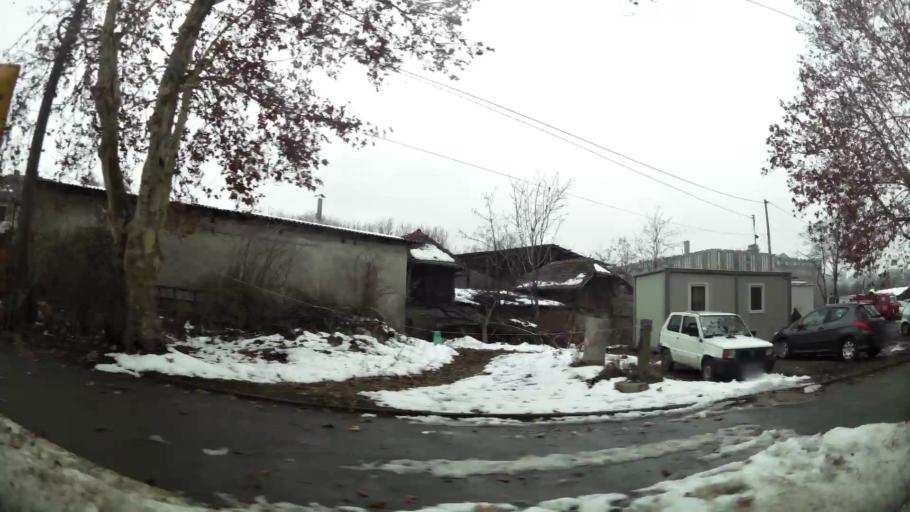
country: RS
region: Central Serbia
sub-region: Belgrade
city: Vozdovac
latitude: 44.7657
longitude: 20.4915
